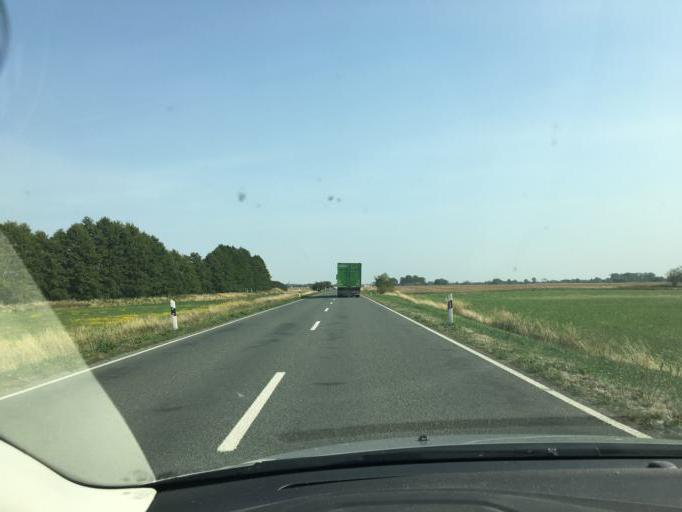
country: DE
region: Saxony-Anhalt
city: Plotzky
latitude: 52.0054
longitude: 11.8036
